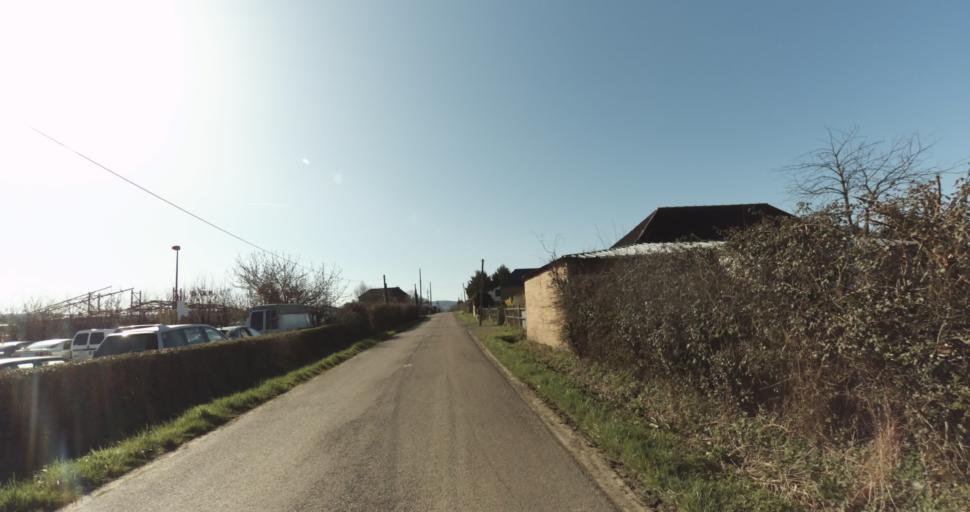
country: FR
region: Lower Normandy
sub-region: Departement du Calvados
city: Saint-Pierre-sur-Dives
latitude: 48.9797
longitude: 0.0347
